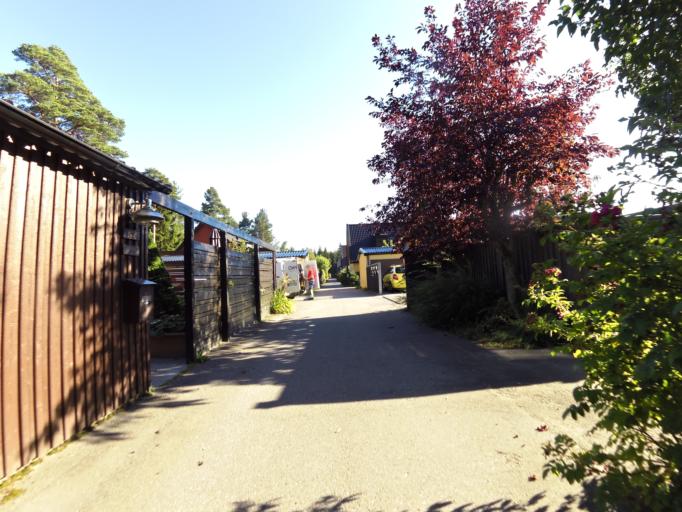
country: SE
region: Gaevleborg
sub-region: Gavle Kommun
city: Gavle
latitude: 60.6542
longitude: 17.1464
